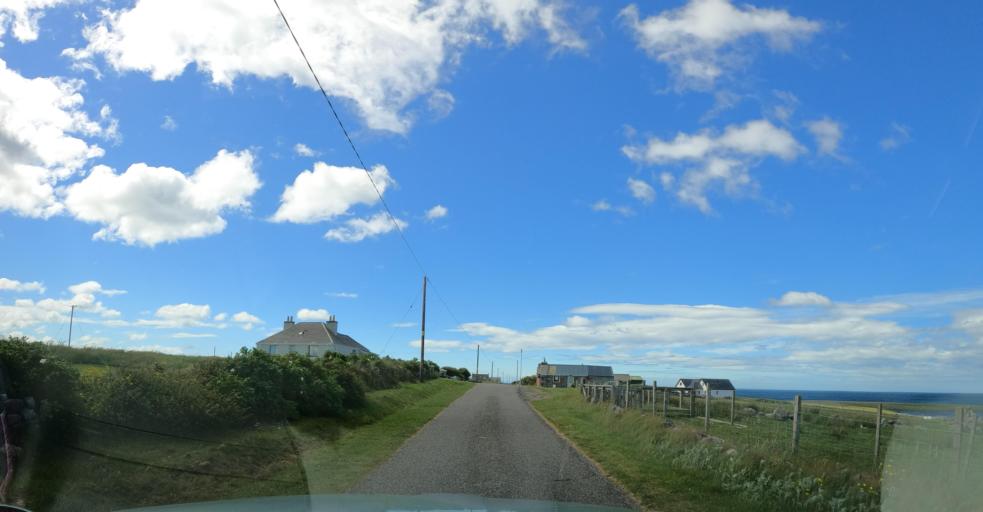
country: GB
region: Scotland
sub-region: Eilean Siar
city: Isle of Lewis
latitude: 58.3568
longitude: -6.5557
